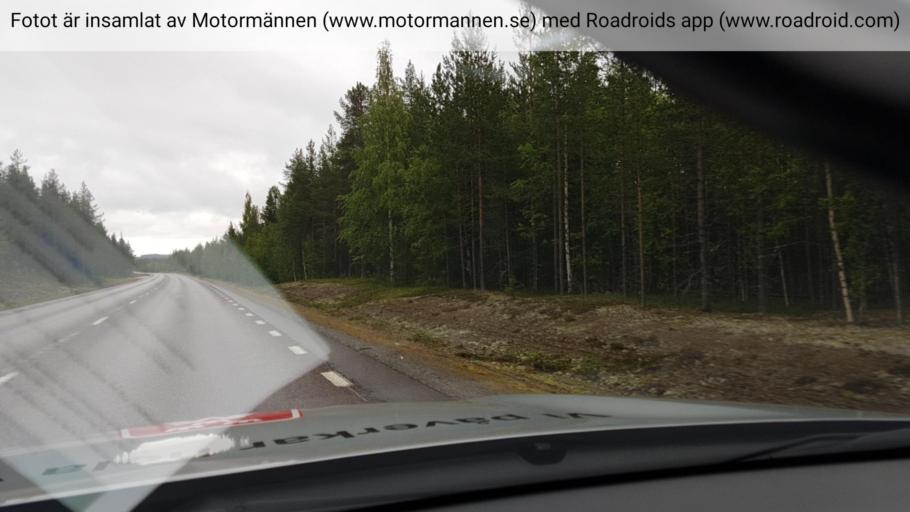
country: SE
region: Norrbotten
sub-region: Gallivare Kommun
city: Gaellivare
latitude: 67.1140
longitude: 20.7838
